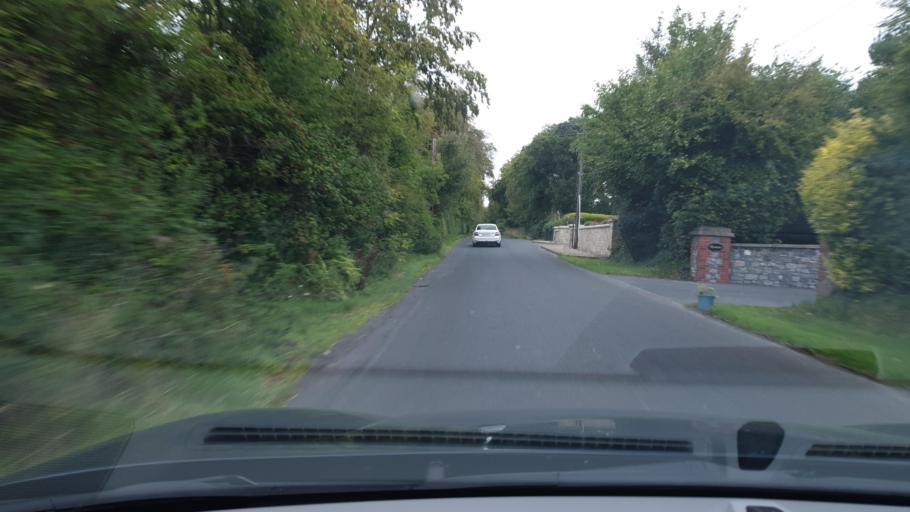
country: IE
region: Leinster
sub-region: An Mhi
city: Dunshaughlin
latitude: 53.5297
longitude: -6.5396
